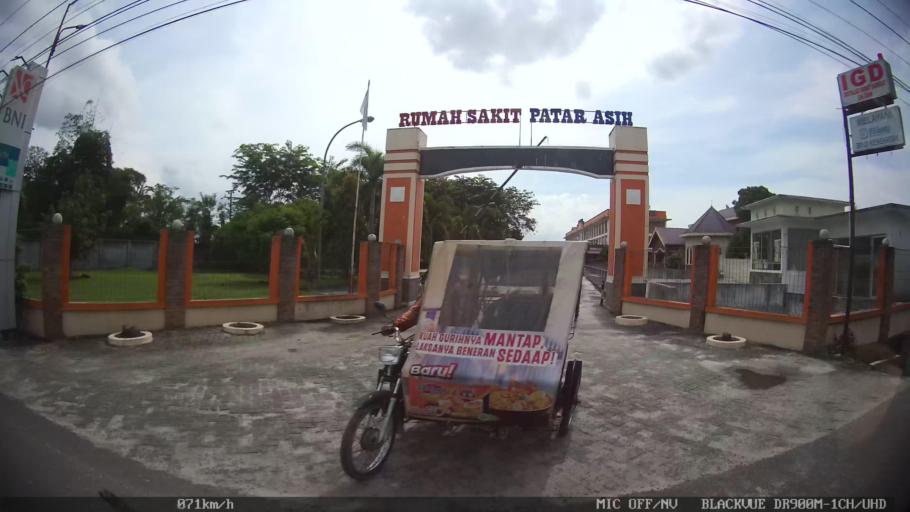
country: ID
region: North Sumatra
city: Percut
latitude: 3.5893
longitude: 98.8592
